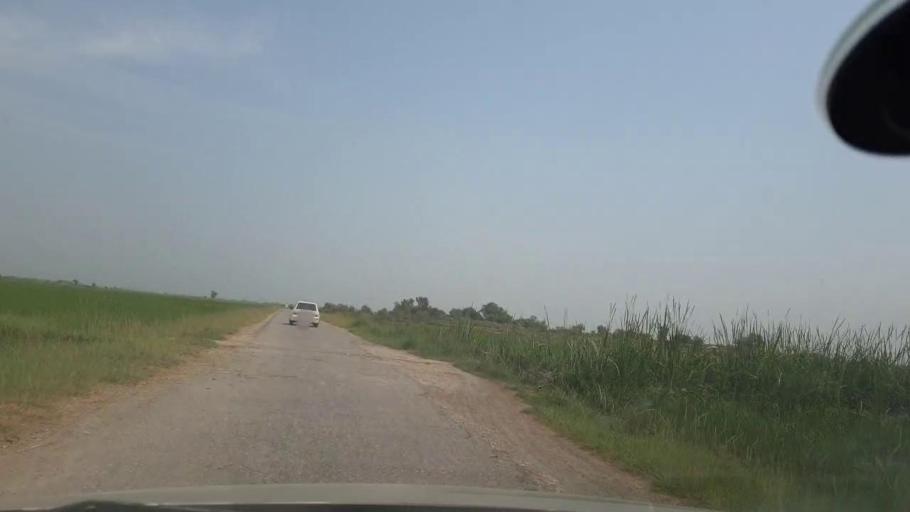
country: PK
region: Sindh
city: Jacobabad
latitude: 28.1417
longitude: 68.3578
